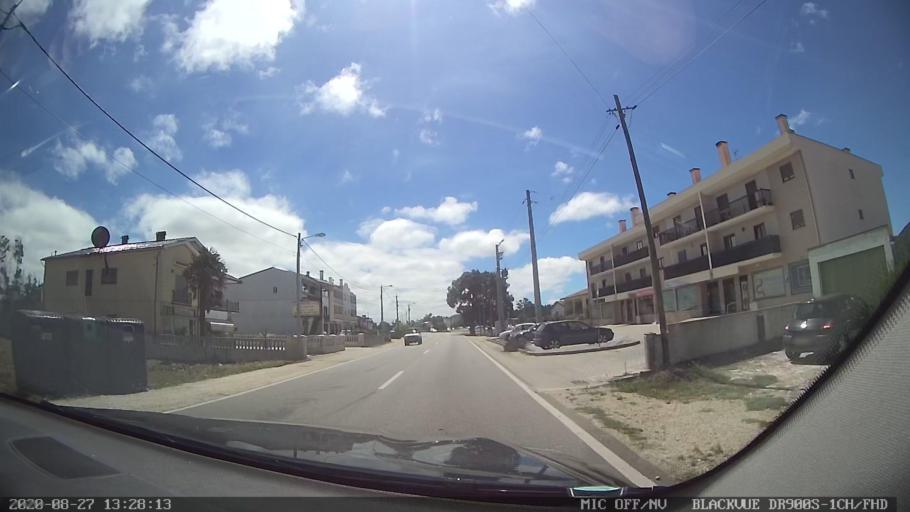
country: PT
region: Aveiro
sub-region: Vagos
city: Vagos
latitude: 40.5227
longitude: -8.6793
